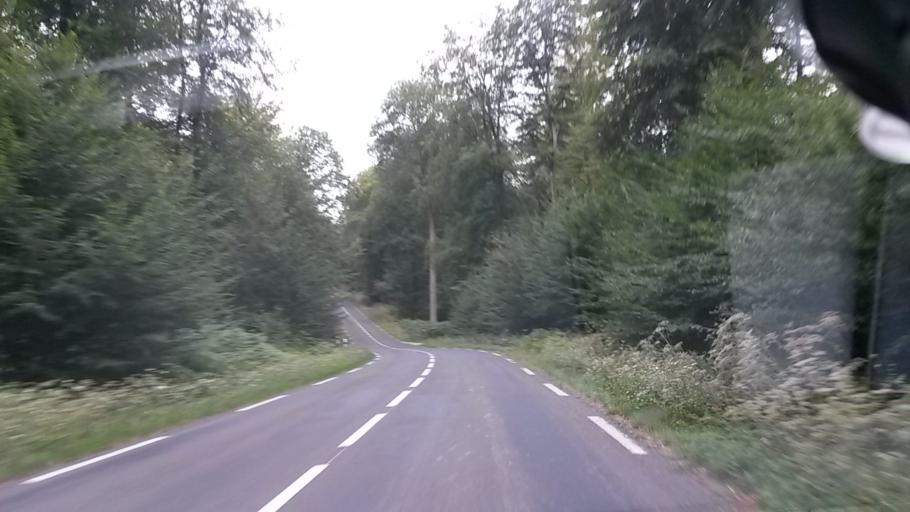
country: FR
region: Haute-Normandie
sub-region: Departement de l'Eure
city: Charleval
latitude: 49.3829
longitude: 1.4693
